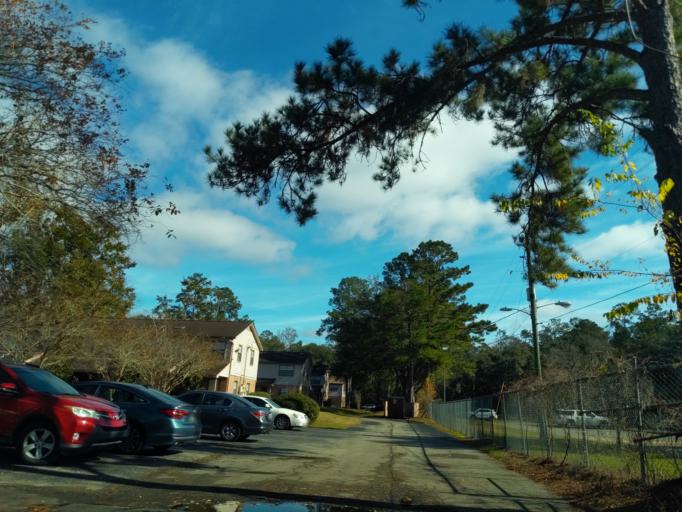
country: US
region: Florida
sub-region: Leon County
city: Tallahassee
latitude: 30.4770
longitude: -84.3226
